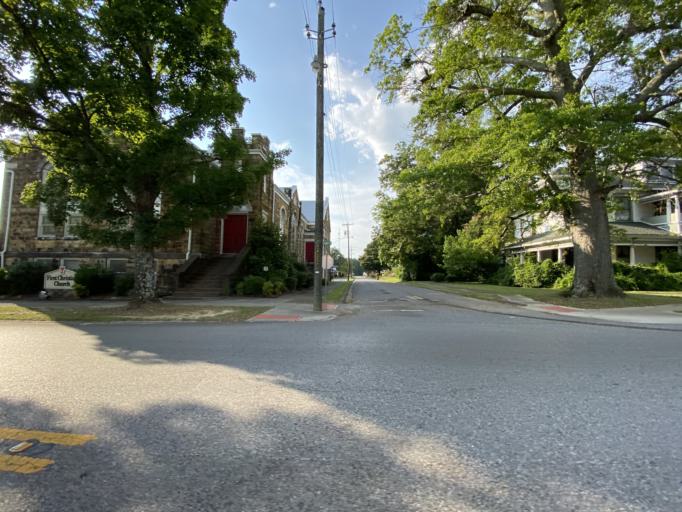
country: US
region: Alabama
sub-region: Morgan County
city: Hartselle
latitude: 34.4447
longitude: -86.9309
